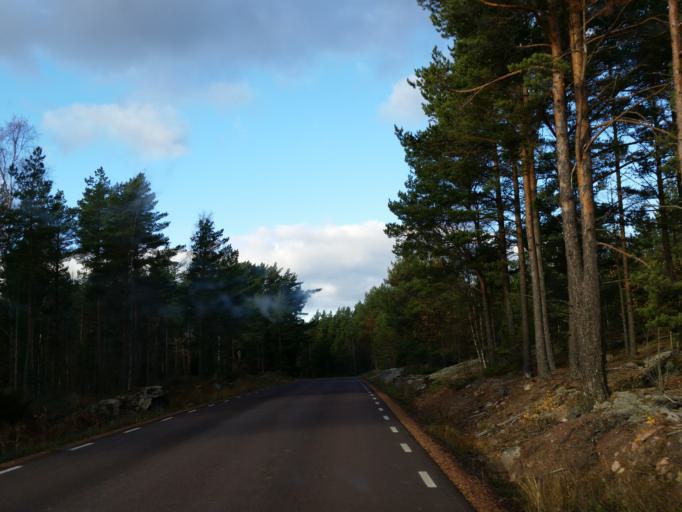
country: AX
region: Alands skaergard
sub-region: Foegloe
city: Foegloe
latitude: 60.0352
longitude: 20.5492
